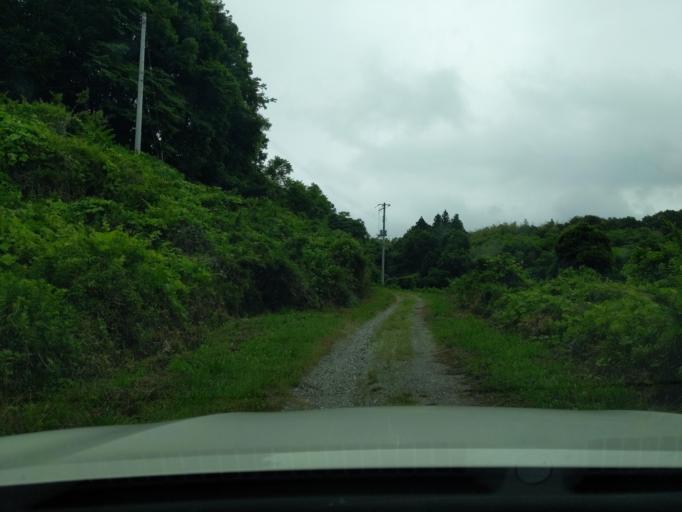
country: JP
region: Fukushima
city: Koriyama
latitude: 37.4017
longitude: 140.4342
